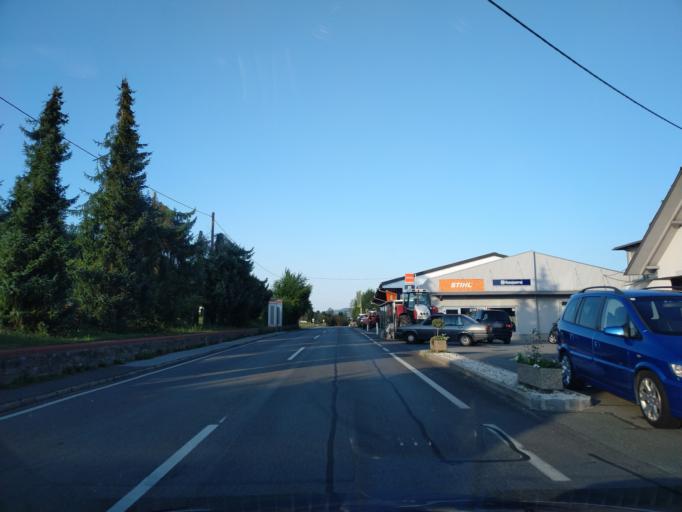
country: AT
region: Styria
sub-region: Politischer Bezirk Deutschlandsberg
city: Wies
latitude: 46.7229
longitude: 15.2786
